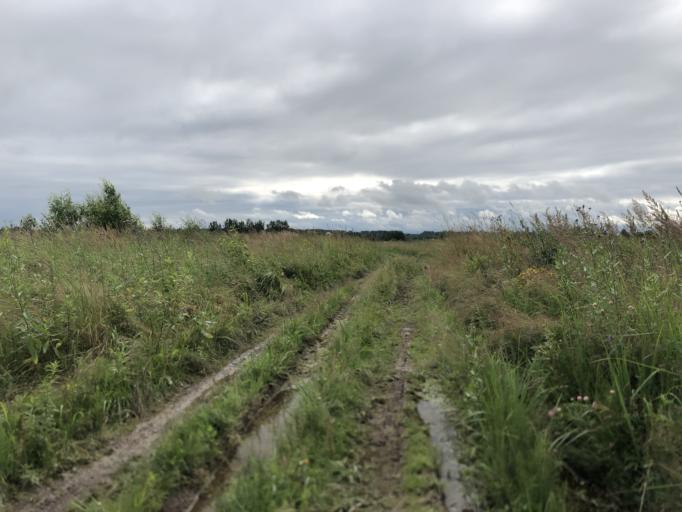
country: RU
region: Tverskaya
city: Rzhev
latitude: 56.2367
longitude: 34.3847
